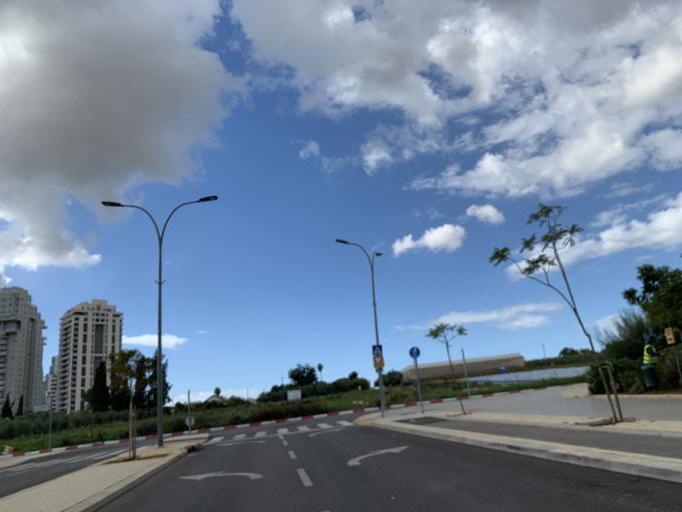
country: IL
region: Central District
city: Hod HaSharon
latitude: 32.1639
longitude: 34.8982
